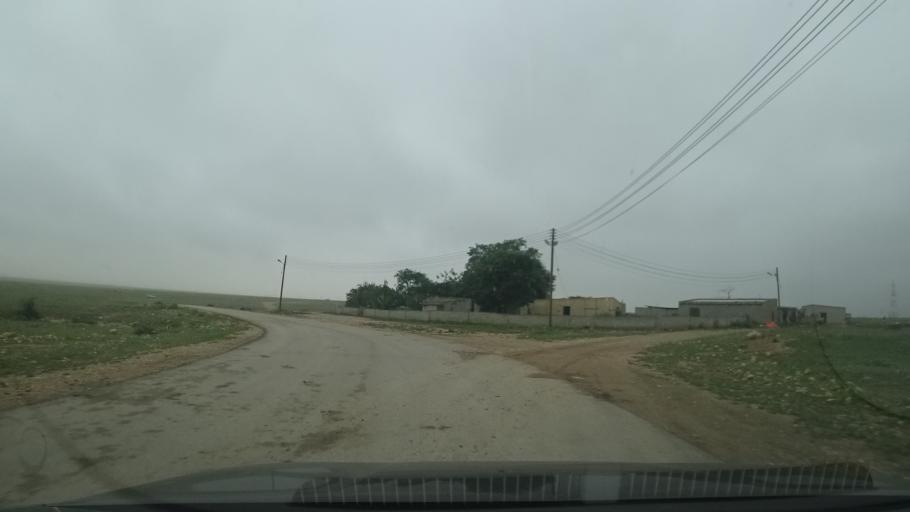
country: OM
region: Zufar
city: Salalah
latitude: 17.0243
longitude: 53.9849
